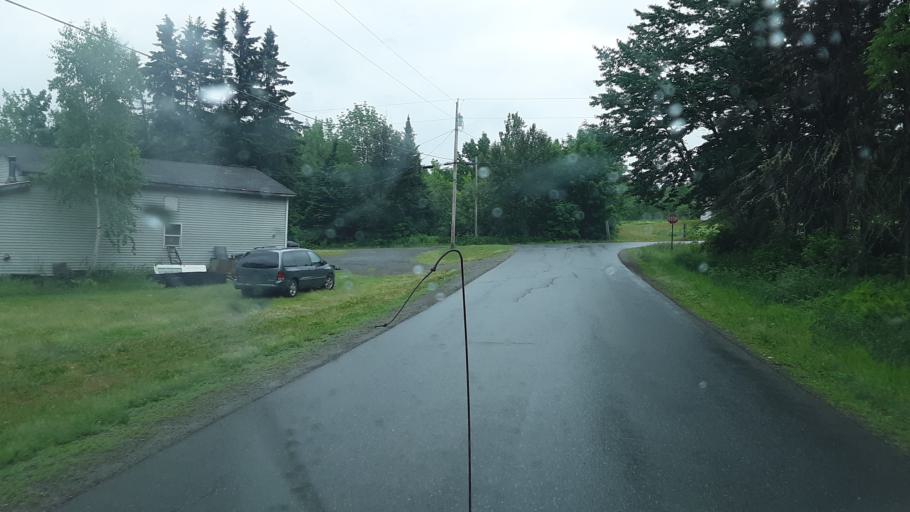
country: US
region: Maine
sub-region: Aroostook County
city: Presque Isle
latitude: 46.6818
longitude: -68.2162
